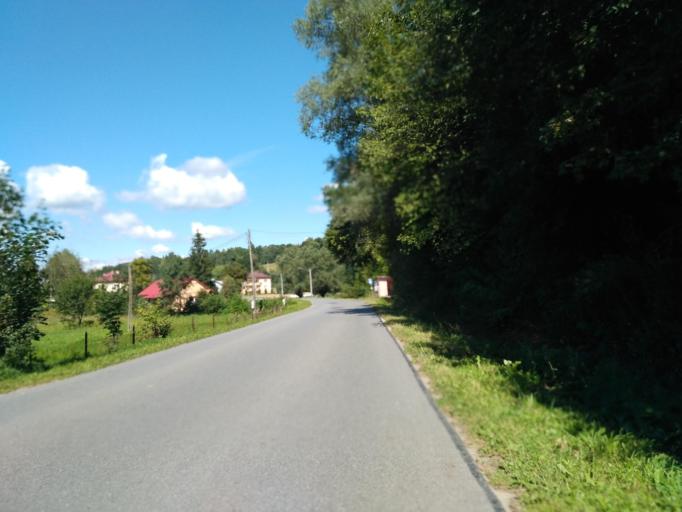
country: PL
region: Subcarpathian Voivodeship
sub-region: Powiat jasielski
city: Skolyszyn
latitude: 49.7936
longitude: 21.3268
